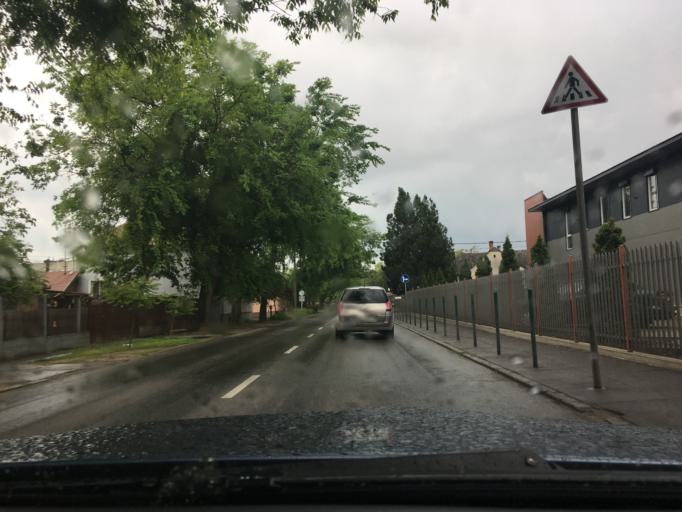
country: HU
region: Hajdu-Bihar
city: Debrecen
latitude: 47.5231
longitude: 21.6594
